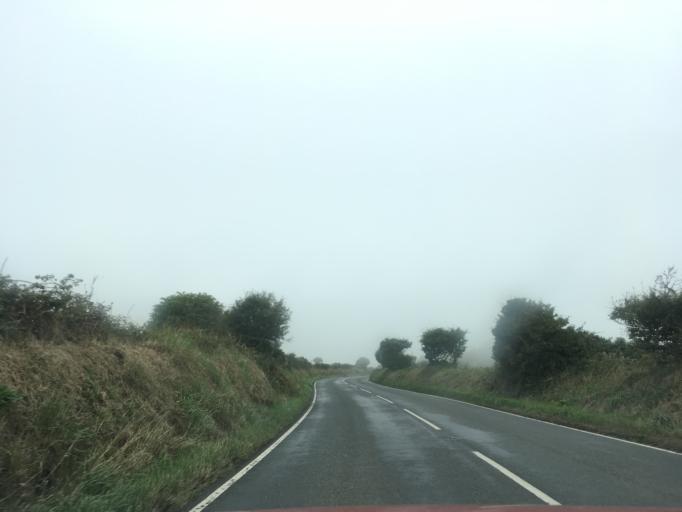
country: GB
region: Wales
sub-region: Pembrokeshire
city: Saint David's
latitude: 51.8804
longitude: -5.2332
